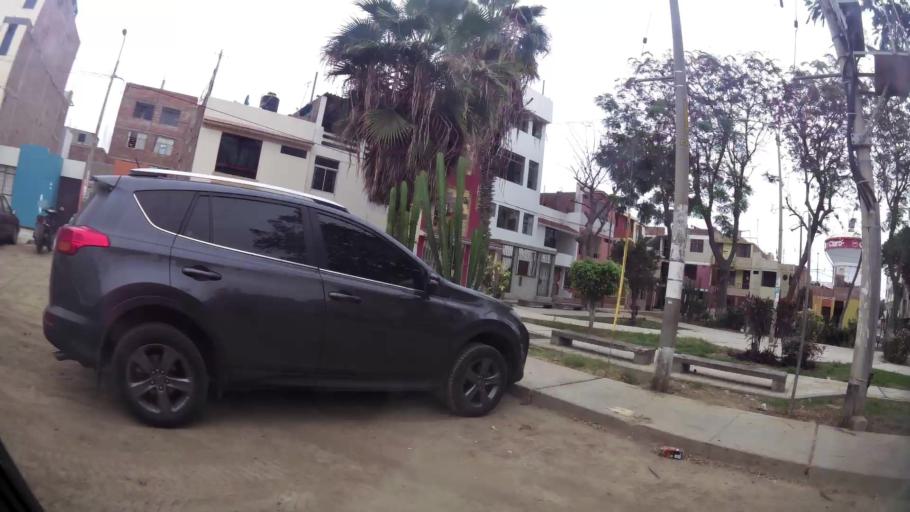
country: PE
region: La Libertad
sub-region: Provincia de Trujillo
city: Trujillo
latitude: -8.1220
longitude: -79.0314
